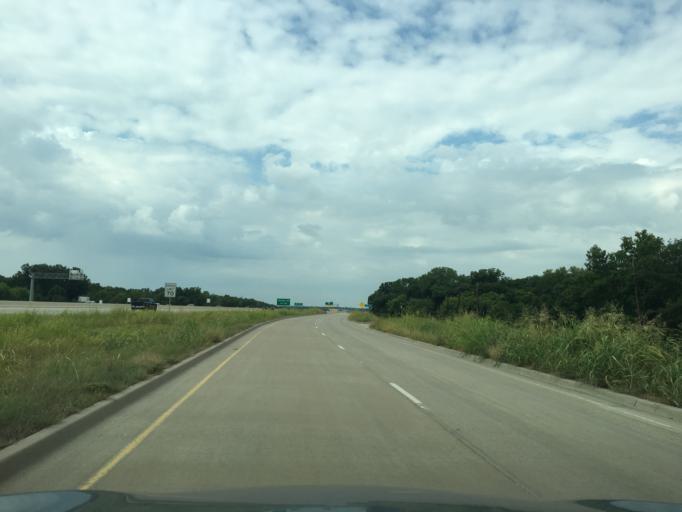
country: US
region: Texas
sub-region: Collin County
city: Melissa
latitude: 33.2594
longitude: -96.6073
